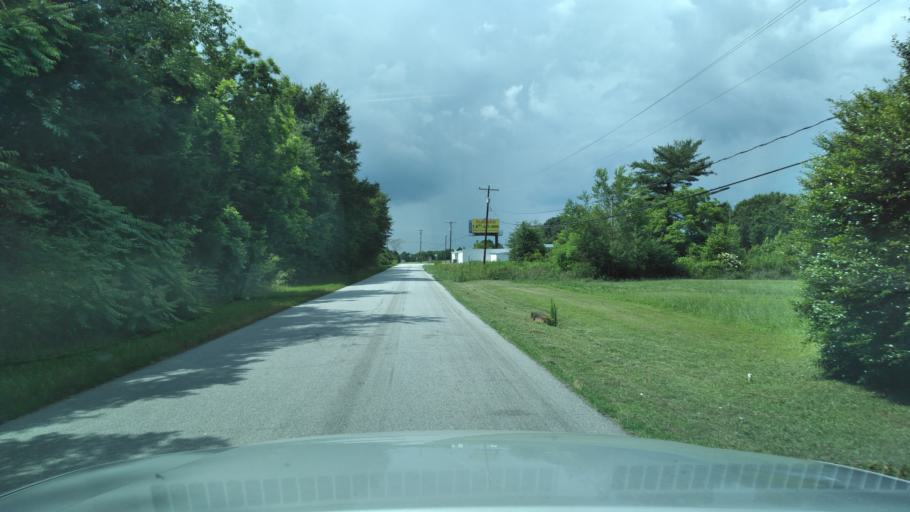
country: US
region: South Carolina
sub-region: Laurens County
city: Laurens
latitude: 34.5681
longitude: -82.0869
